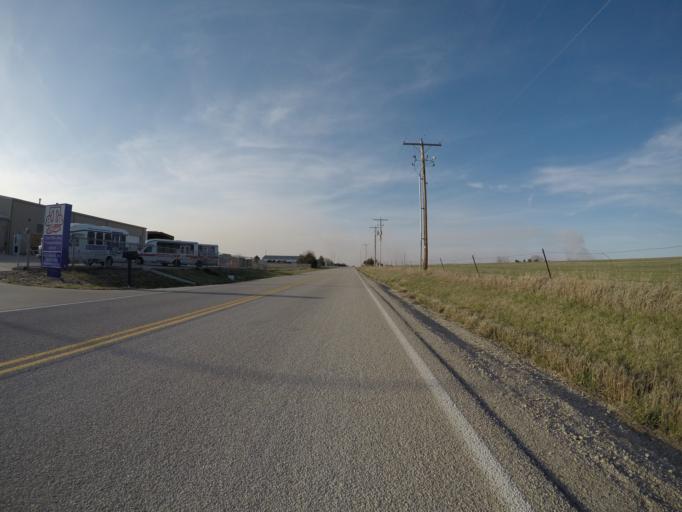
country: US
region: Kansas
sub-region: Riley County
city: Manhattan
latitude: 39.2482
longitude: -96.6538
